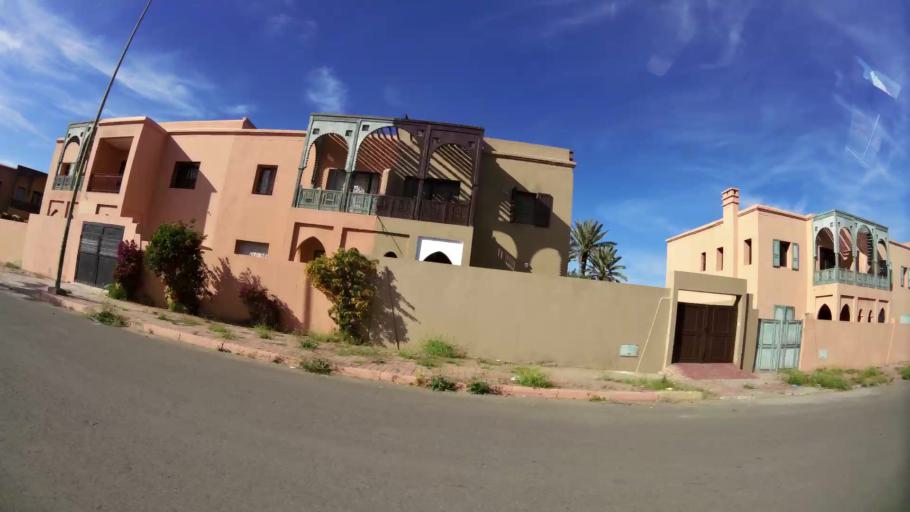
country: MA
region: Marrakech-Tensift-Al Haouz
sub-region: Marrakech
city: Marrakesh
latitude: 31.6744
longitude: -8.0547
